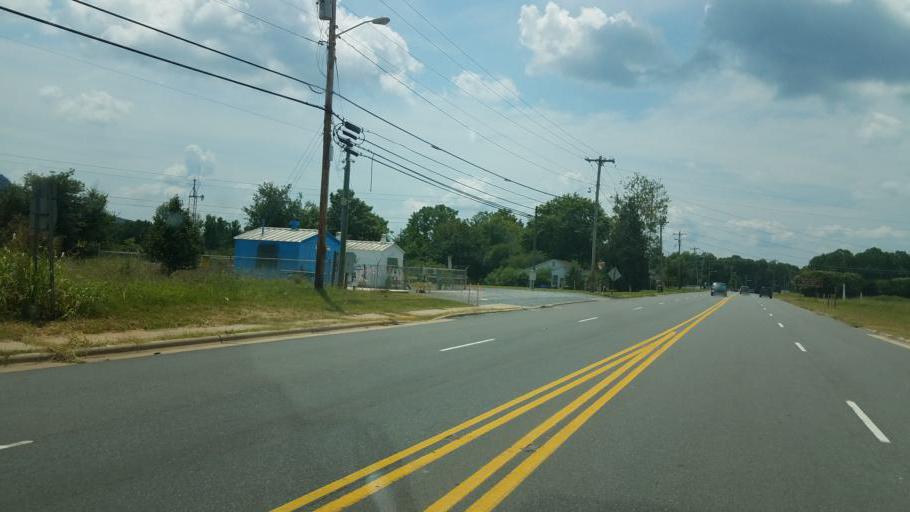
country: US
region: North Carolina
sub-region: Cleveland County
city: Kings Mountain
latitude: 35.2218
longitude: -81.3339
